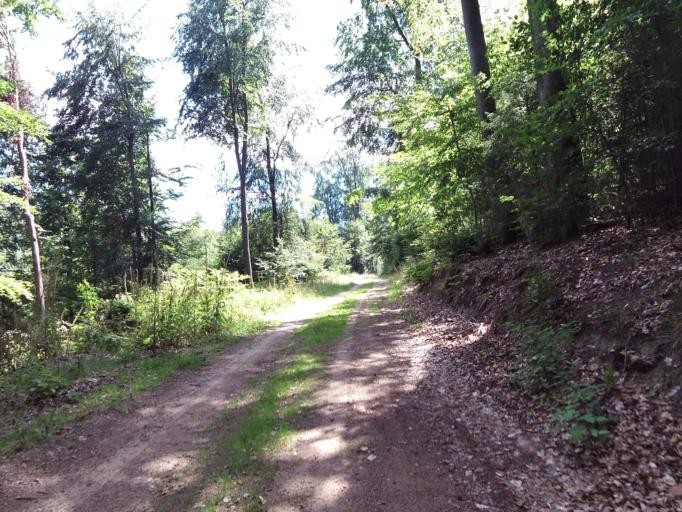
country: DE
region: Rheinland-Pfalz
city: Altleiningen
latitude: 49.4676
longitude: 8.0655
